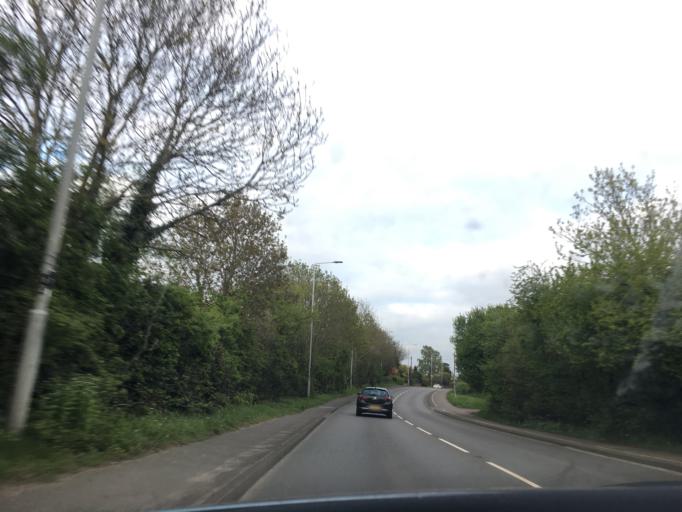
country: GB
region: England
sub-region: Leicestershire
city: Oadby
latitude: 52.6322
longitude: -1.0556
